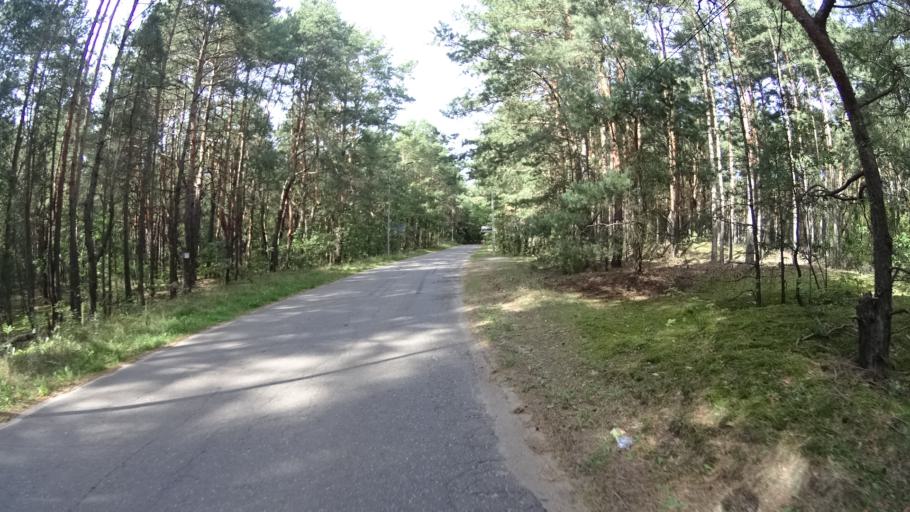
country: PL
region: Masovian Voivodeship
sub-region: Powiat legionowski
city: Serock
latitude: 52.4798
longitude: 21.0861
